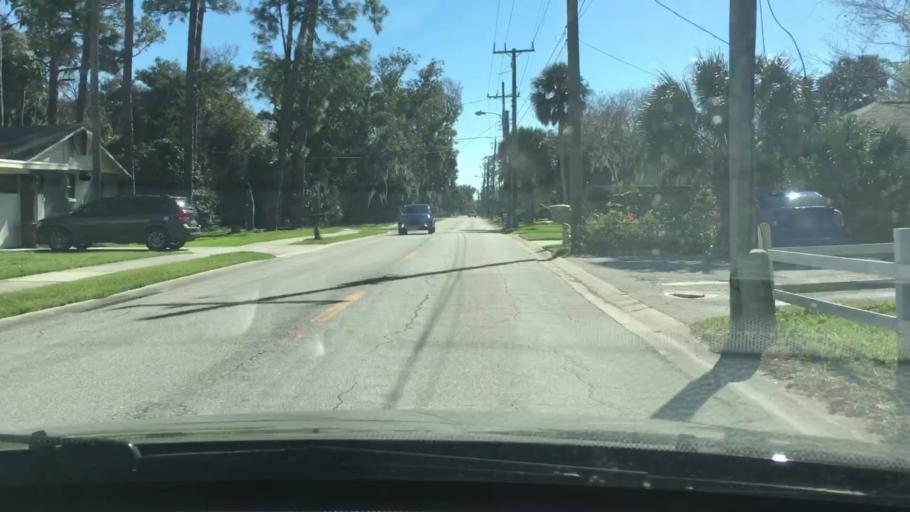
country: US
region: Florida
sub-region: Volusia County
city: Ormond Beach
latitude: 29.2781
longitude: -81.0673
